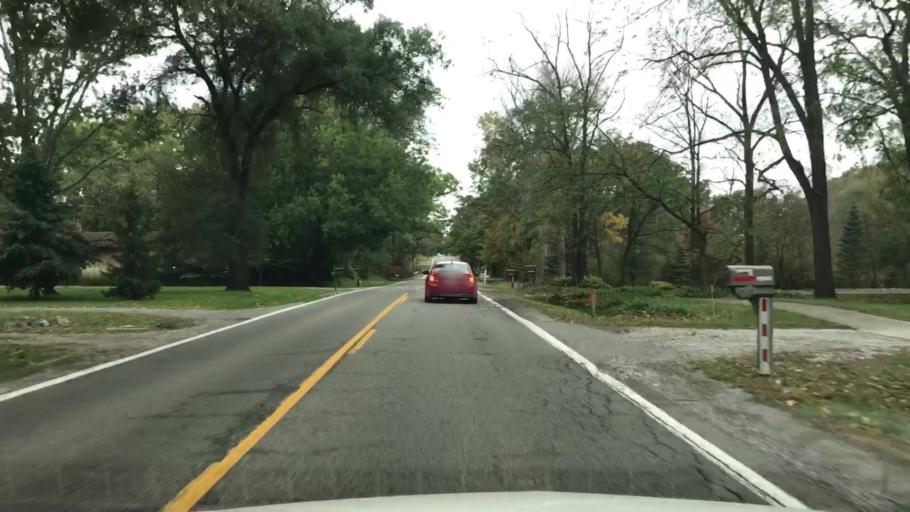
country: US
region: Michigan
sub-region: Macomb County
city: Shelby
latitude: 42.6807
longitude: -83.0670
